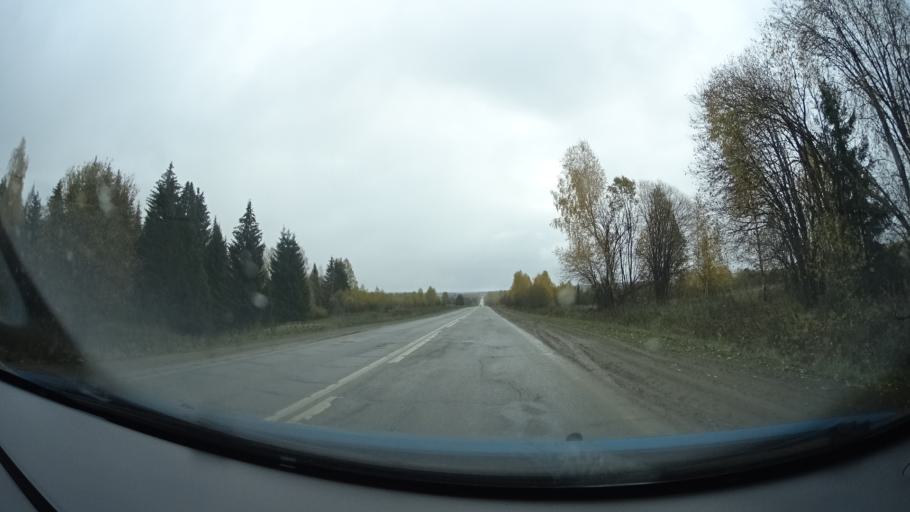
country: RU
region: Perm
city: Chernushka
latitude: 56.7554
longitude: 56.1461
